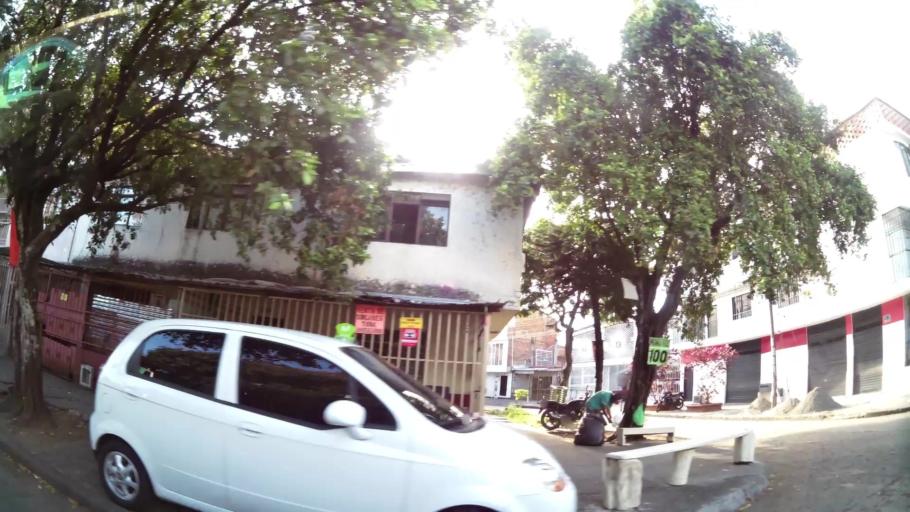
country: CO
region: Valle del Cauca
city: Cali
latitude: 3.4311
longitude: -76.5223
